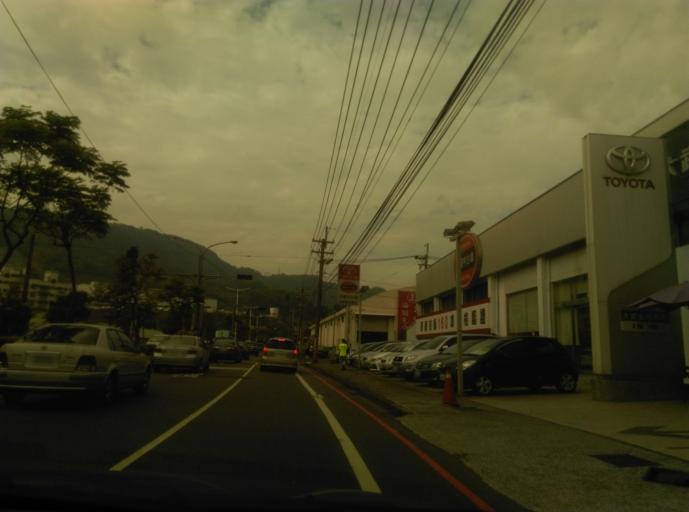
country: TW
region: Taiwan
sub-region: Keelung
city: Keelung
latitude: 25.1513
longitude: 121.6989
